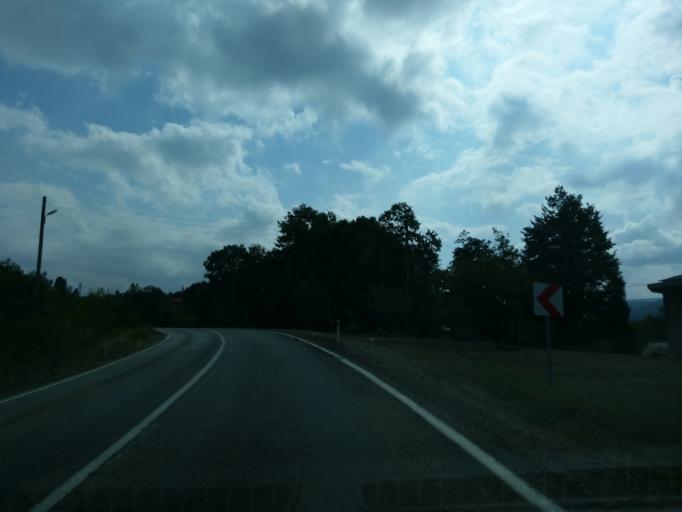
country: TR
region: Sinop
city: Erfelek
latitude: 41.9461
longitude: 34.7831
